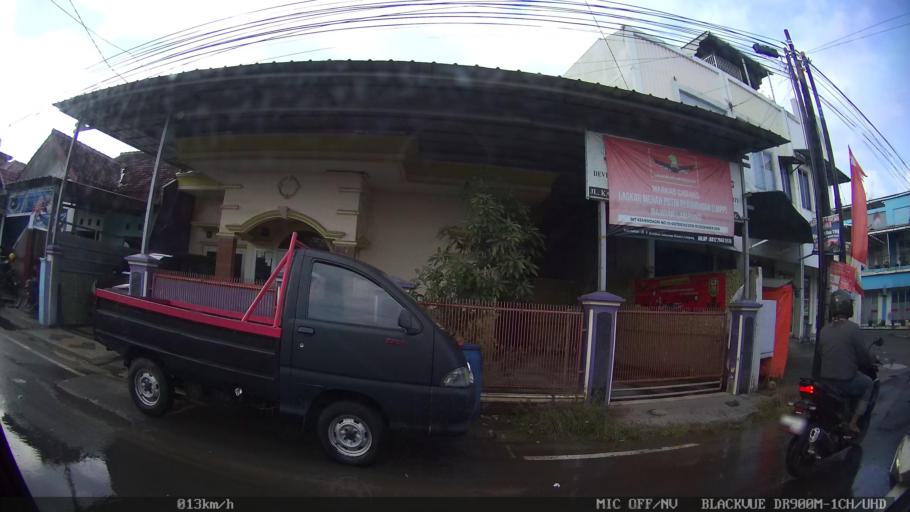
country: ID
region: Lampung
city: Kedaton
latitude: -5.3908
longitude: 105.3016
